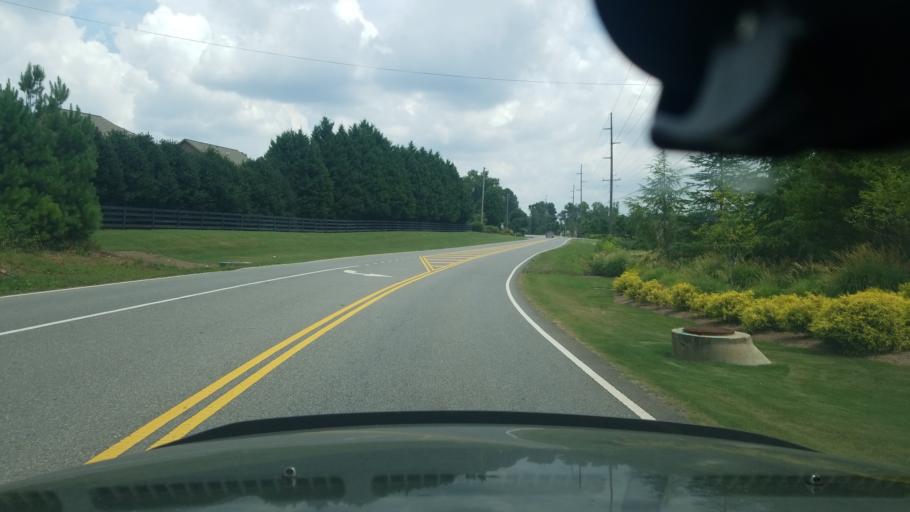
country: US
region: Georgia
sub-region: Fulton County
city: Milton
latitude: 34.1975
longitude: -84.2527
